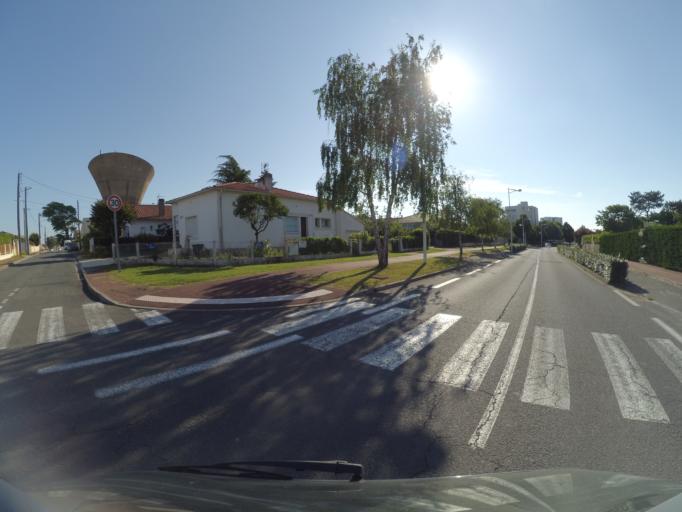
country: FR
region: Poitou-Charentes
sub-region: Departement de la Charente-Maritime
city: Royan
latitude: 45.6351
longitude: -1.0245
